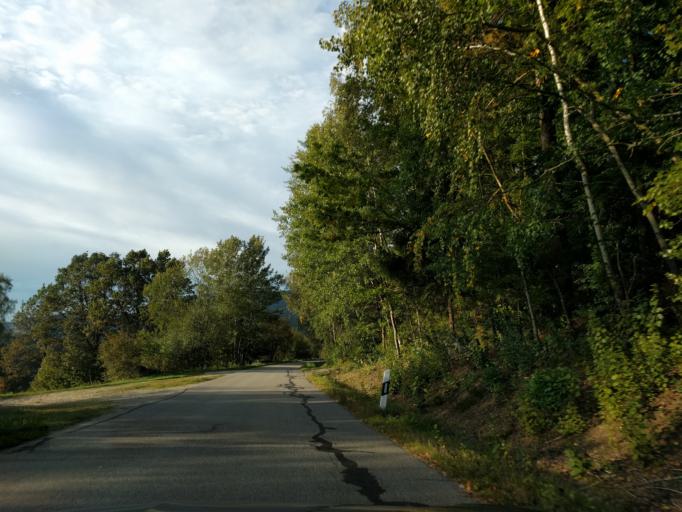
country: DE
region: Bavaria
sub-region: Upper Palatinate
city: Hohenwarth
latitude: 49.1935
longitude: 12.9317
